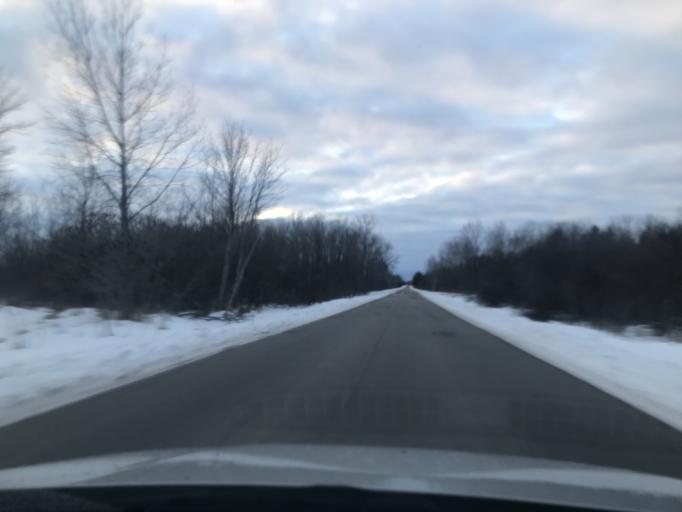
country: US
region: Wisconsin
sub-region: Marinette County
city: Peshtigo
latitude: 45.1646
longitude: -87.7413
